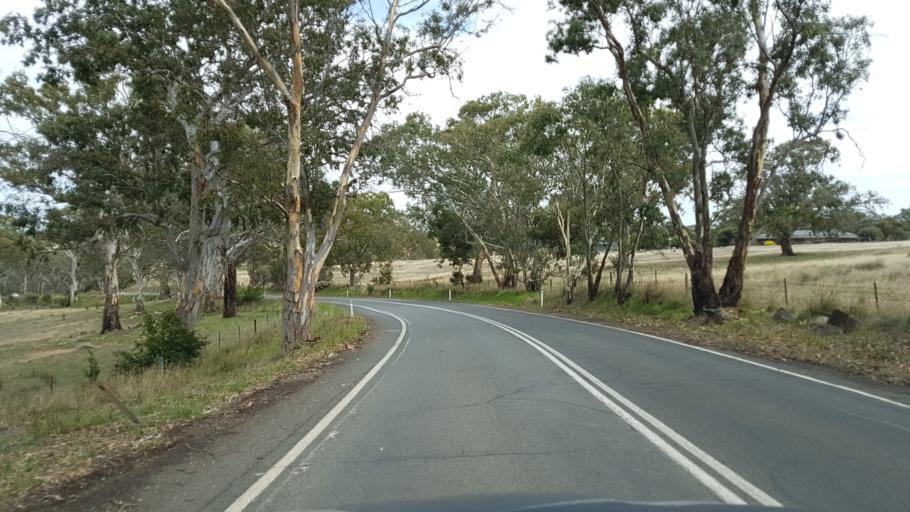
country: AU
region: South Australia
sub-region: Mount Barker
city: Nairne
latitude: -35.0419
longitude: 138.9355
